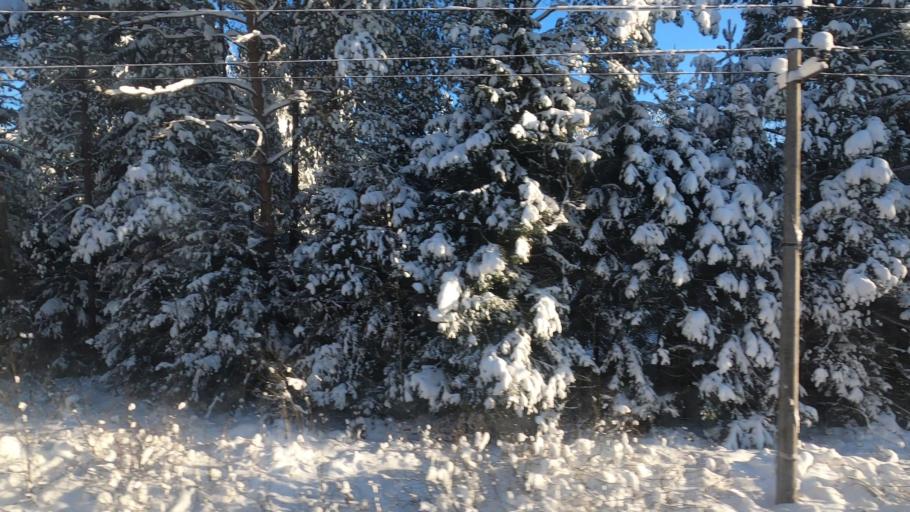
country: RU
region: Moskovskaya
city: Zhukovka
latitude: 56.4927
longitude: 37.5512
